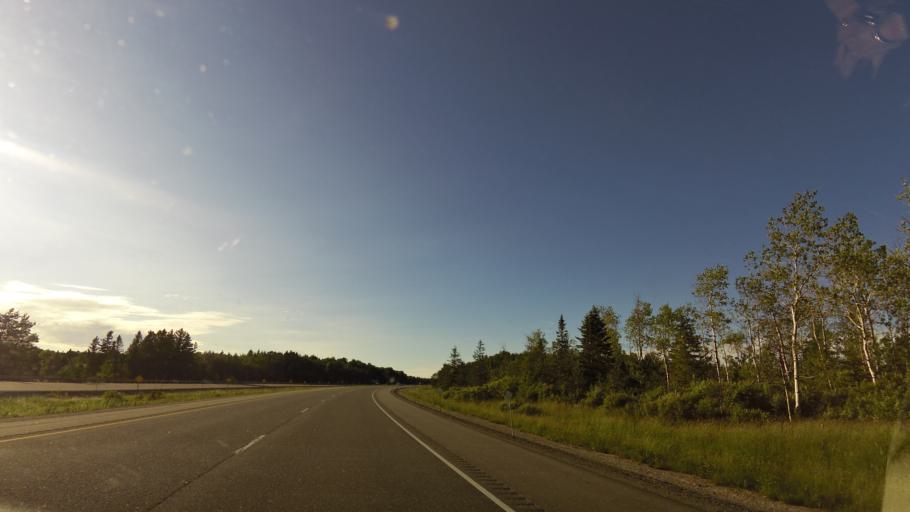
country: CA
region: Ontario
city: Barrie
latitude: 44.5285
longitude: -79.7447
